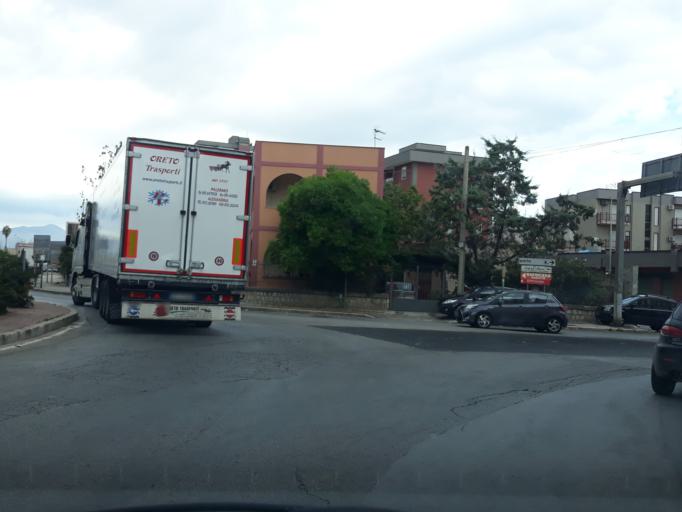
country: IT
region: Sicily
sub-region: Palermo
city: Ciaculli
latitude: 38.0939
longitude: 13.4030
